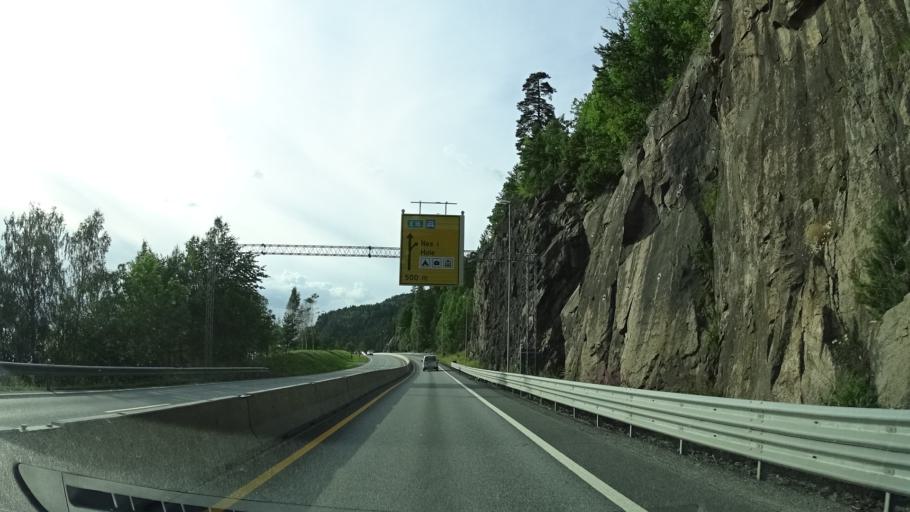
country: NO
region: Buskerud
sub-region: Hole
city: Vik
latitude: 59.9868
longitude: 10.3059
